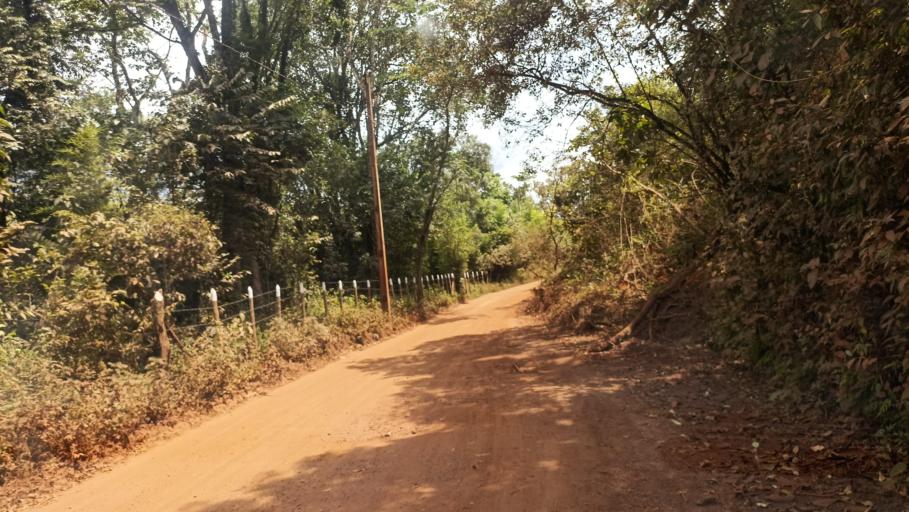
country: BR
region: Minas Gerais
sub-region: Itabirito
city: Itabirito
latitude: -20.3357
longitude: -43.7667
